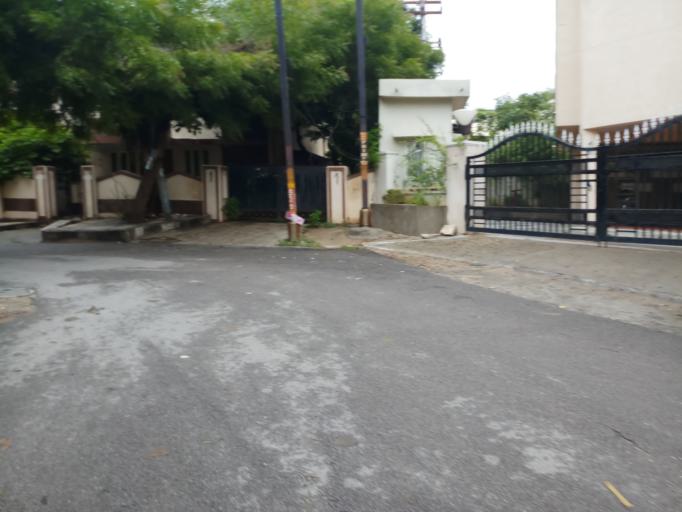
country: IN
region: Telangana
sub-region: Rangareddi
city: Gaddi Annaram
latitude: 17.3679
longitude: 78.5189
